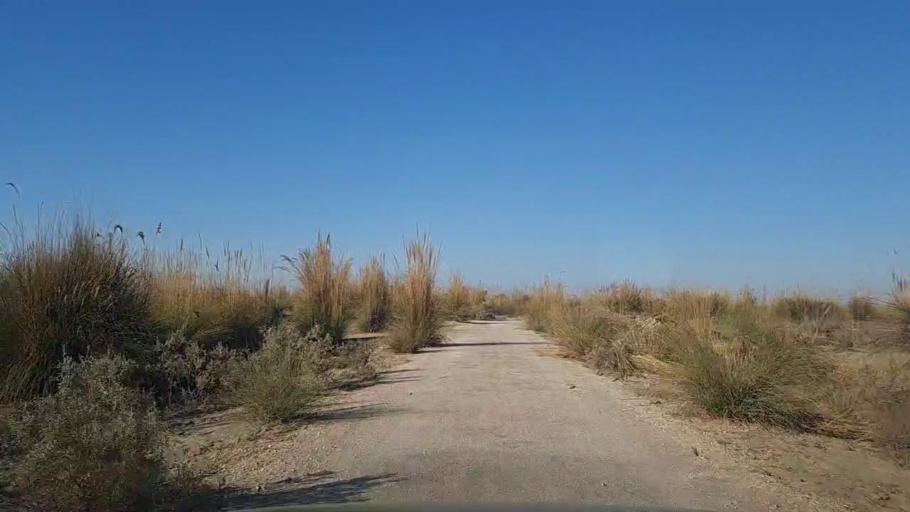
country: PK
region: Sindh
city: Khadro
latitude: 26.2492
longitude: 68.8643
